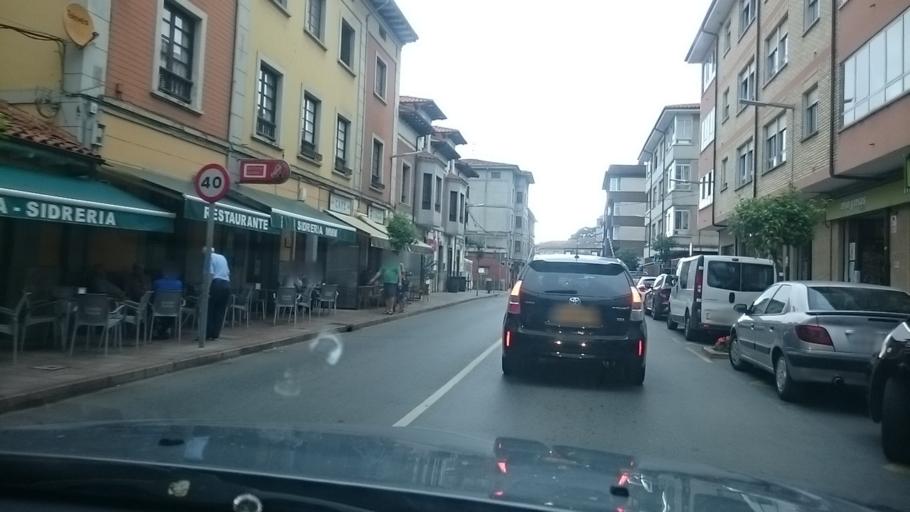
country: ES
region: Asturias
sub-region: Province of Asturias
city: Carrena
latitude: 43.4238
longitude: -4.8635
